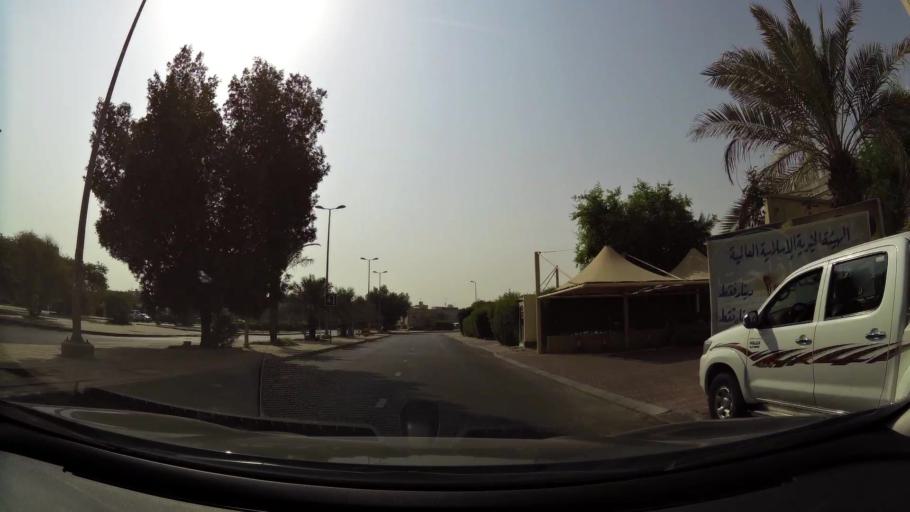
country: KW
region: Al Asimah
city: Ar Rabiyah
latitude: 29.2906
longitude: 47.8934
